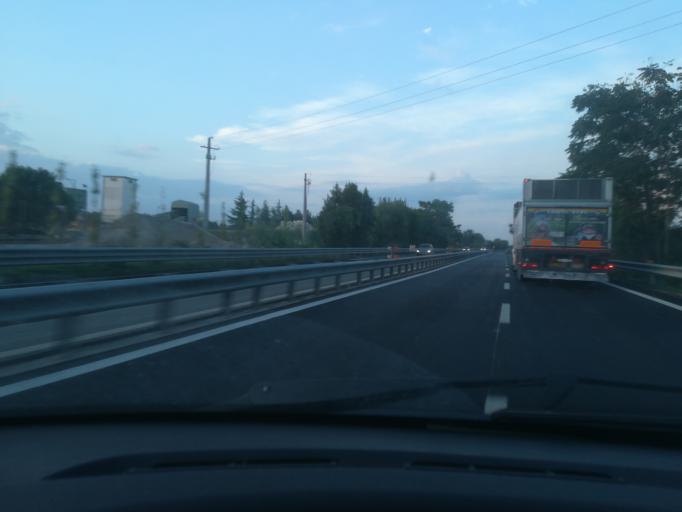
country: IT
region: The Marches
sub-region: Provincia di Macerata
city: Zona Industriale
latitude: 43.2600
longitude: 13.4696
